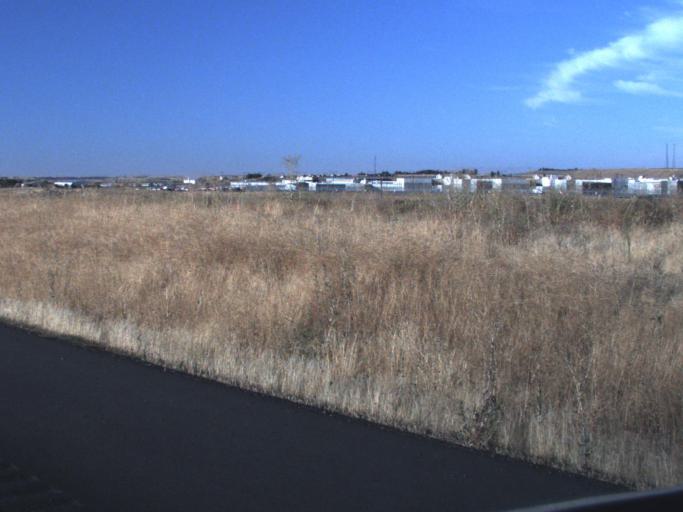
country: US
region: Washington
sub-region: Franklin County
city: Connell
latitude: 46.6840
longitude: -118.8414
